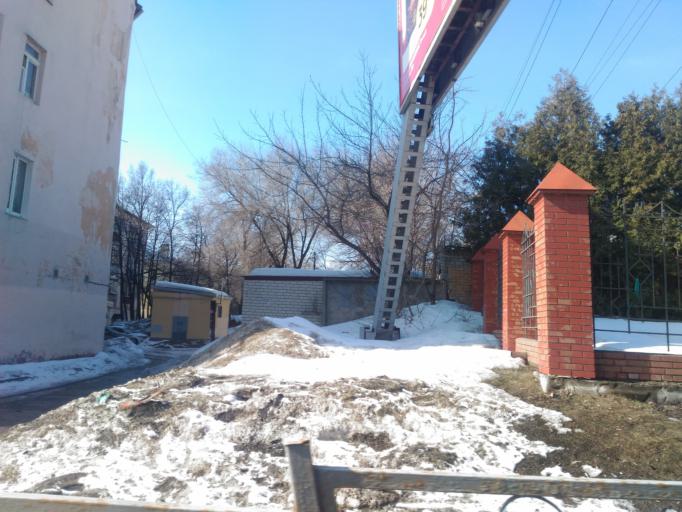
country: RU
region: Ulyanovsk
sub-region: Ulyanovskiy Rayon
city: Ulyanovsk
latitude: 54.3065
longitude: 48.3892
